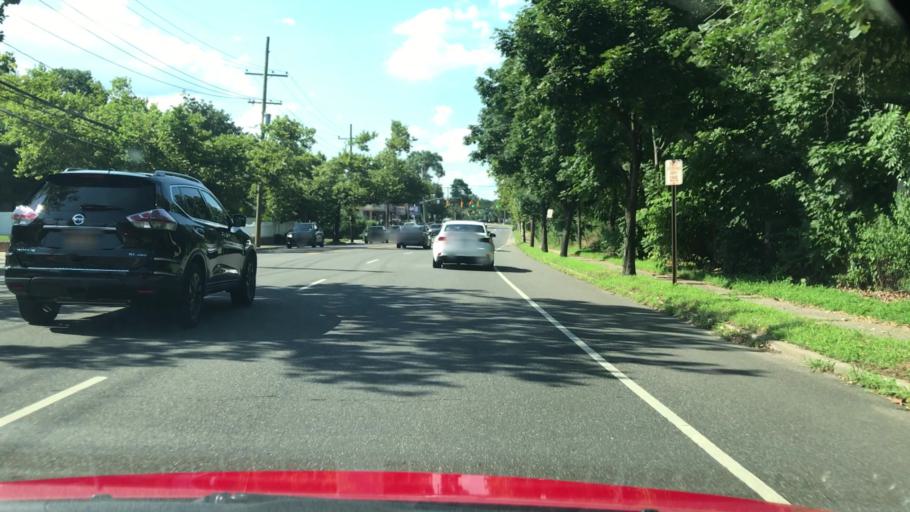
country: US
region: New York
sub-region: Nassau County
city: Lynbrook
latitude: 40.6656
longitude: -73.6602
